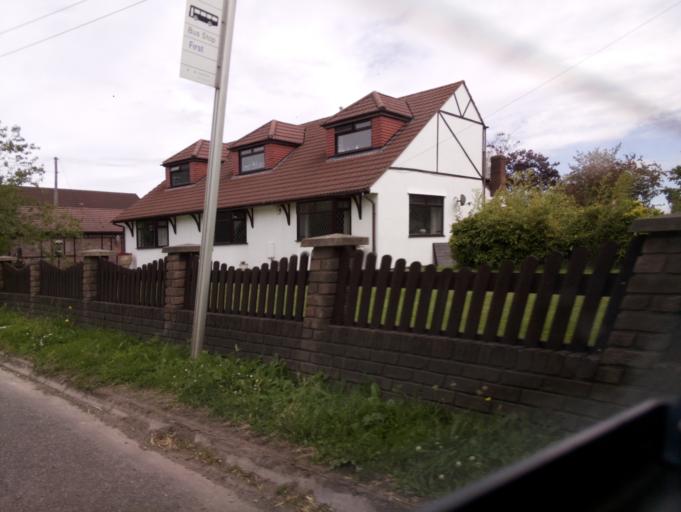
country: GB
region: England
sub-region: North Somerset
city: Kenn
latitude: 51.4073
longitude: -2.8448
